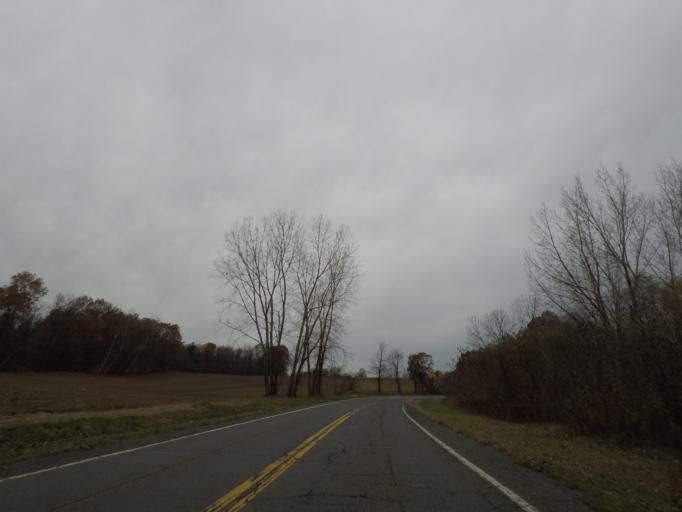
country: US
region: New York
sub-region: Saratoga County
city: Mechanicville
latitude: 42.8512
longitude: -73.6991
